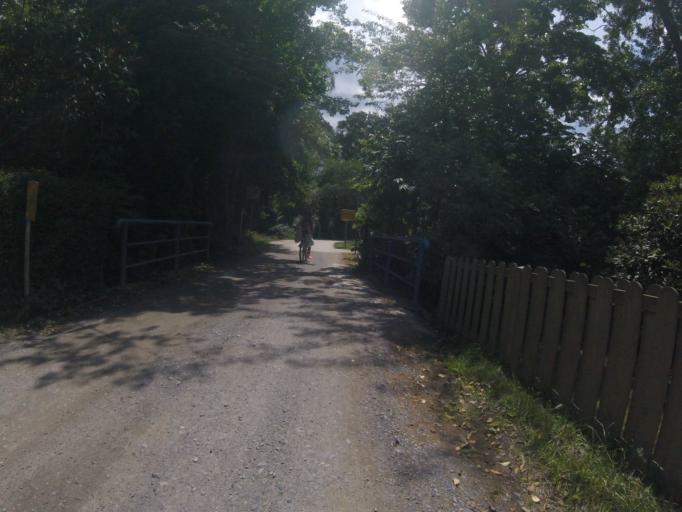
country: DE
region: Brandenburg
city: Bestensee
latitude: 52.2556
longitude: 13.6466
